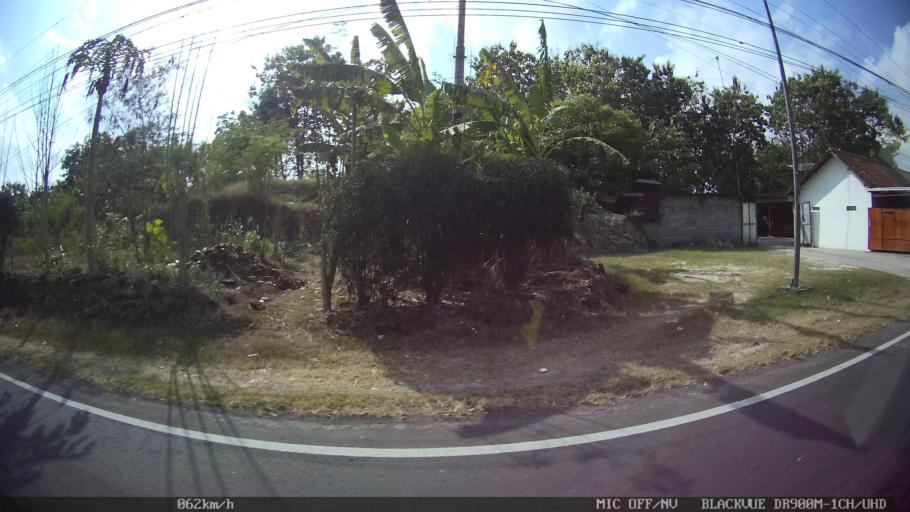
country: ID
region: Daerah Istimewa Yogyakarta
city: Srandakan
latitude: -7.8622
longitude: 110.2114
